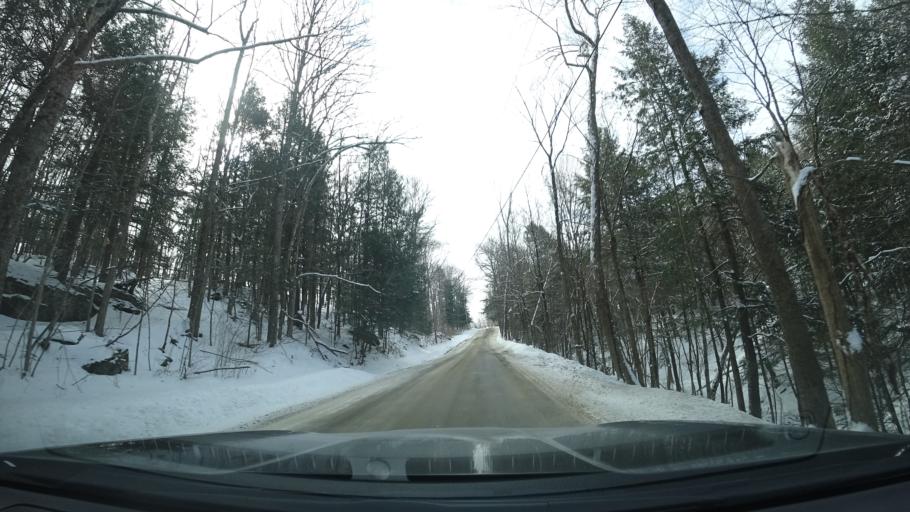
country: US
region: New York
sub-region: Washington County
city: Greenwich
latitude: 43.2211
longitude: -73.3555
